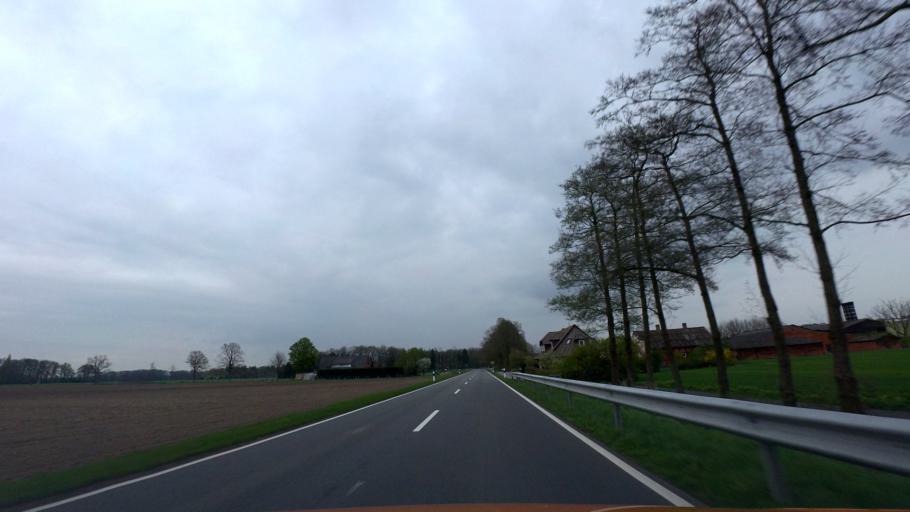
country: DE
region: Lower Saxony
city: Quakenbruck
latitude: 52.6933
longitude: 7.9912
